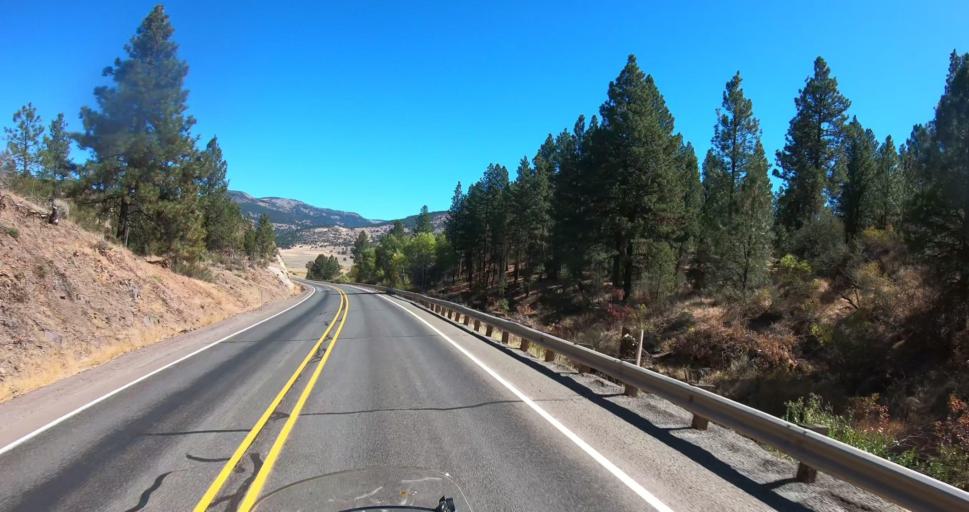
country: US
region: Oregon
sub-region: Lake County
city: Lakeview
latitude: 42.3256
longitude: -120.3105
